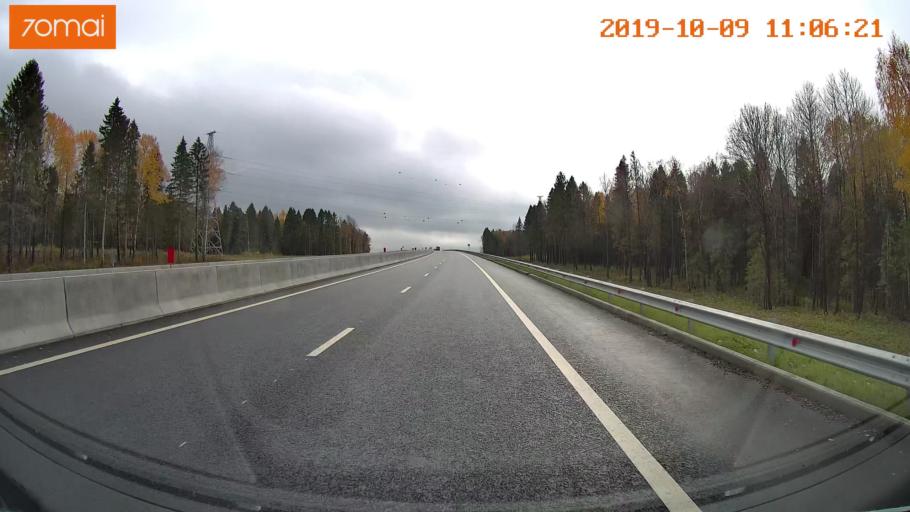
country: RU
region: Vologda
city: Vologda
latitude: 59.1877
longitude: 39.7598
